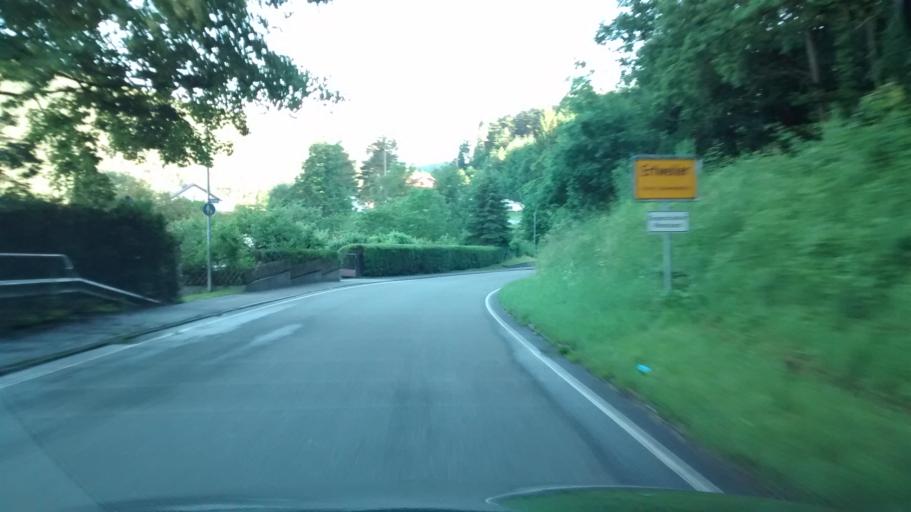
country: DE
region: Rheinland-Pfalz
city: Erfweiler
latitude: 49.1555
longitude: 7.8069
